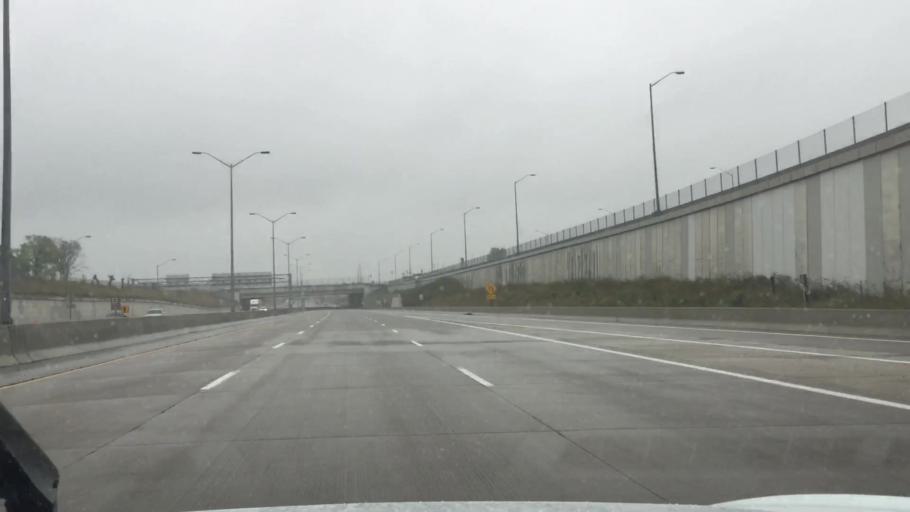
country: CA
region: Ontario
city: Windsor
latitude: 42.2454
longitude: -83.0245
